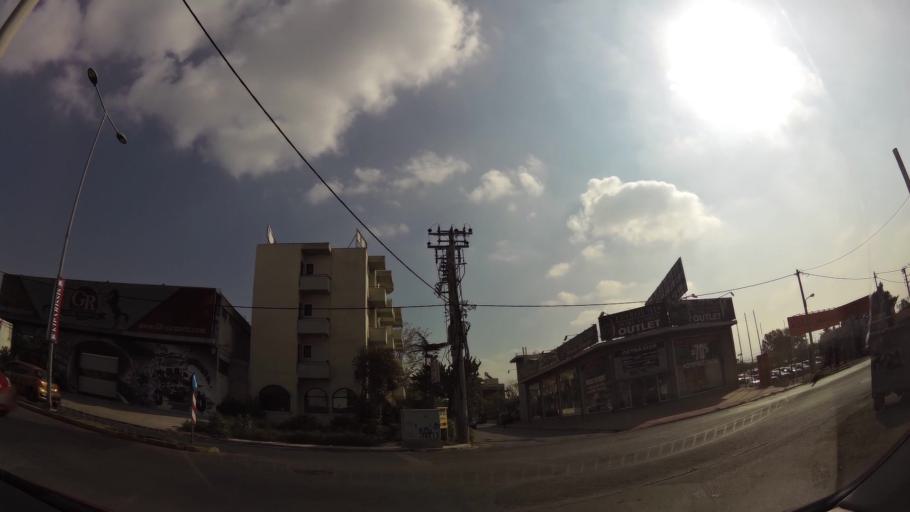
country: GR
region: Attica
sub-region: Nomarchia Dytikis Attikis
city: Zefyri
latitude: 38.0574
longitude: 23.7308
